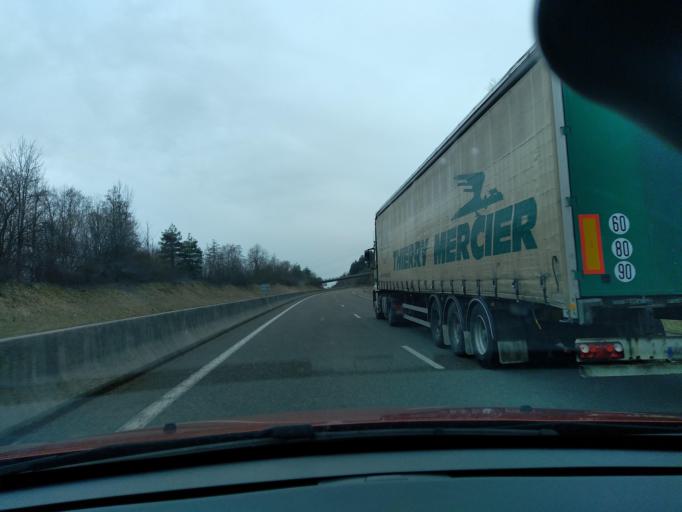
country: FR
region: Rhone-Alpes
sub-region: Departement de l'Ain
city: Martignat
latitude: 46.2123
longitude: 5.6028
